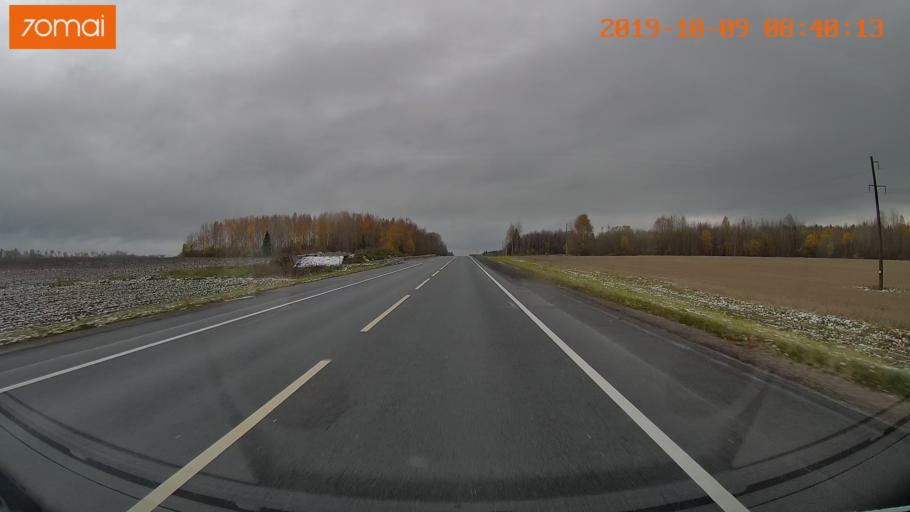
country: RU
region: Vologda
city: Gryazovets
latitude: 58.9832
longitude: 40.1432
